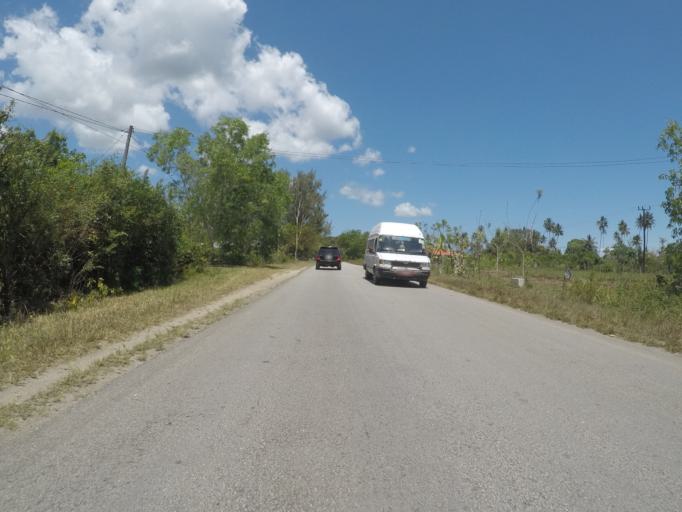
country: TZ
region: Zanzibar Central/South
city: Nganane
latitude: -6.2811
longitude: 39.4341
